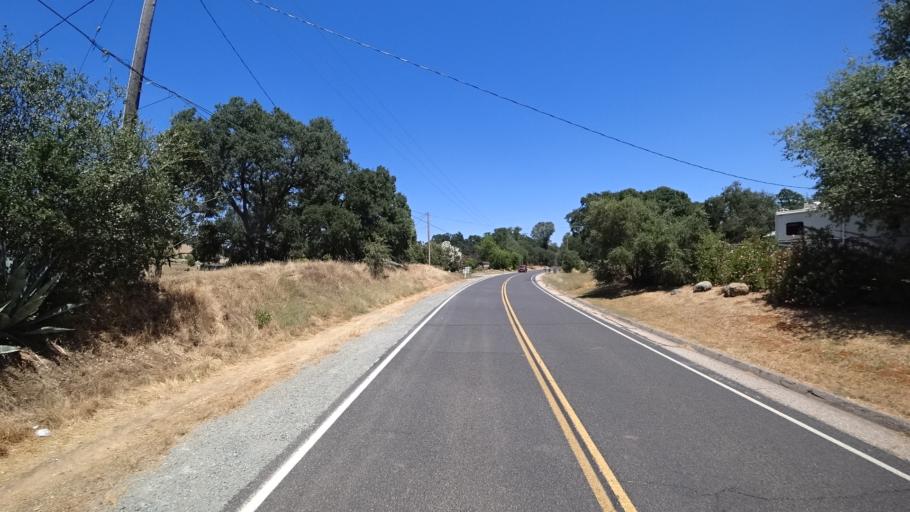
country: US
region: California
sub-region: Calaveras County
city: Rancho Calaveras
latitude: 38.1157
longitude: -120.8640
